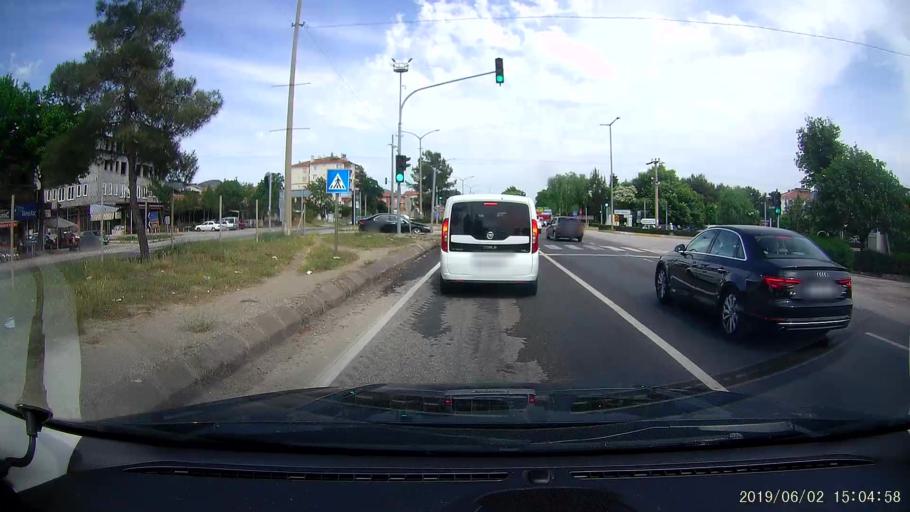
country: TR
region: Corum
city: Osmancik
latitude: 40.9797
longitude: 34.7982
